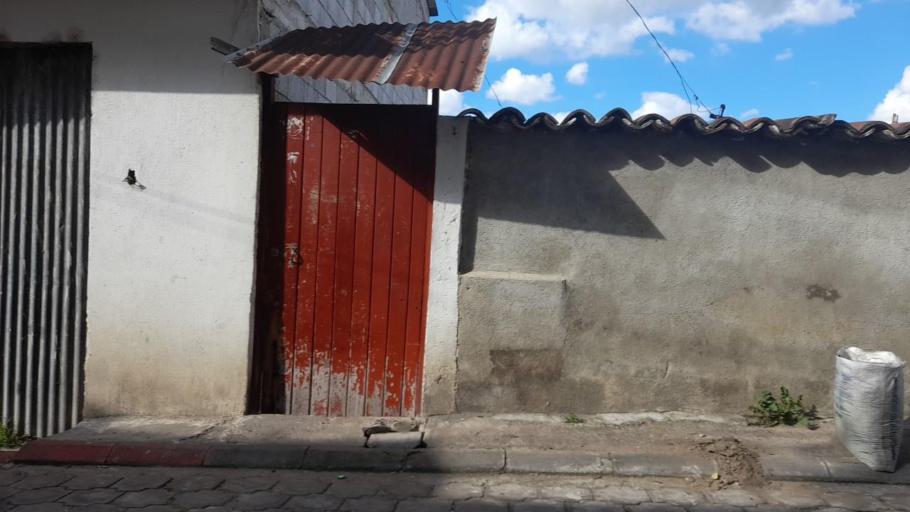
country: GT
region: Quetzaltenango
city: Quetzaltenango
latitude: 14.8290
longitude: -91.5166
